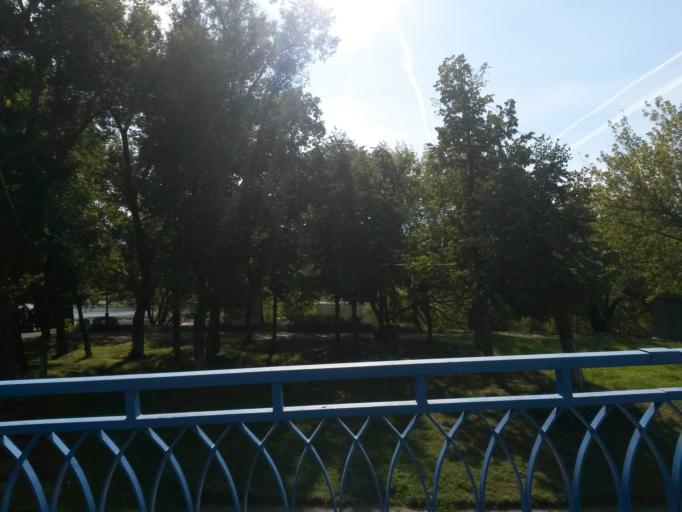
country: RU
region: Jaroslavl
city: Yaroslavl
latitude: 57.6199
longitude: 39.8986
